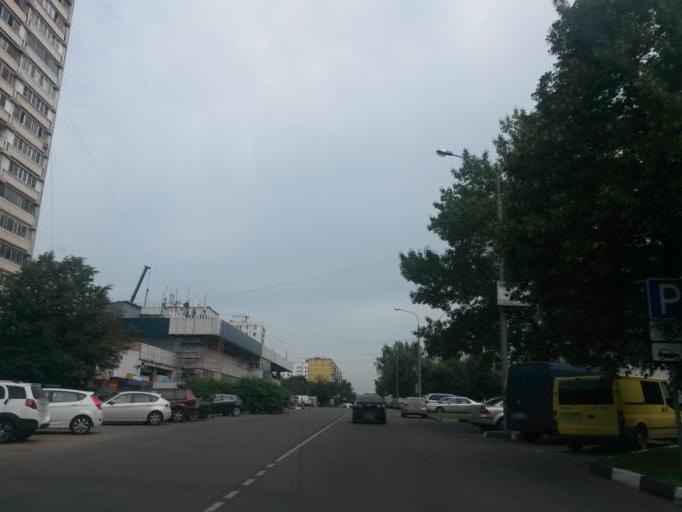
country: RU
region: Moscow
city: Orekhovo-Borisovo
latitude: 55.6082
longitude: 37.7328
